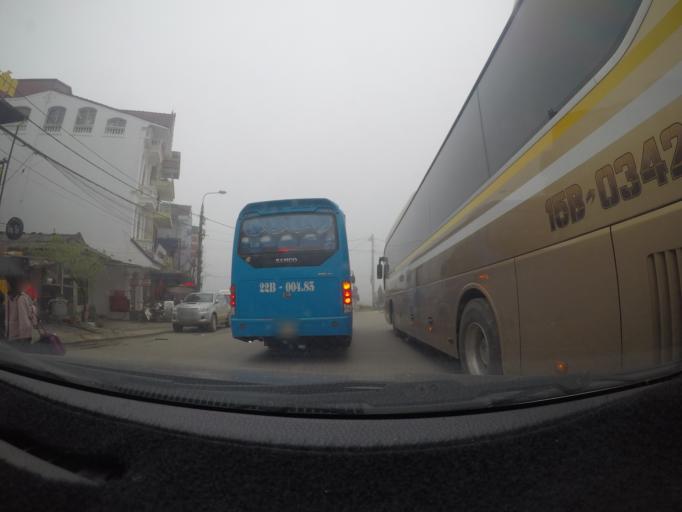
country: VN
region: Lao Cai
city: Sa Pa
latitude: 22.3396
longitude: 103.8478
